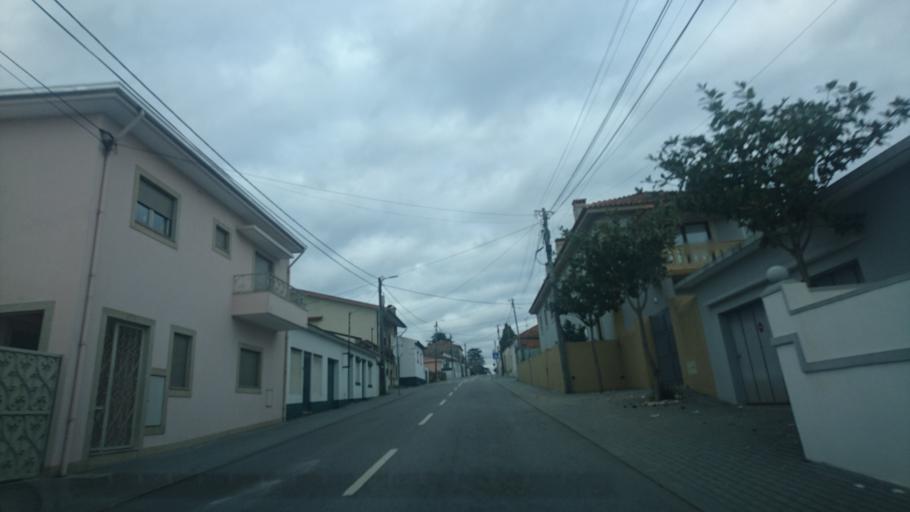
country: PT
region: Aveiro
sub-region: Santa Maria da Feira
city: Pacos de Brandao
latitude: 40.9674
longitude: -8.5915
